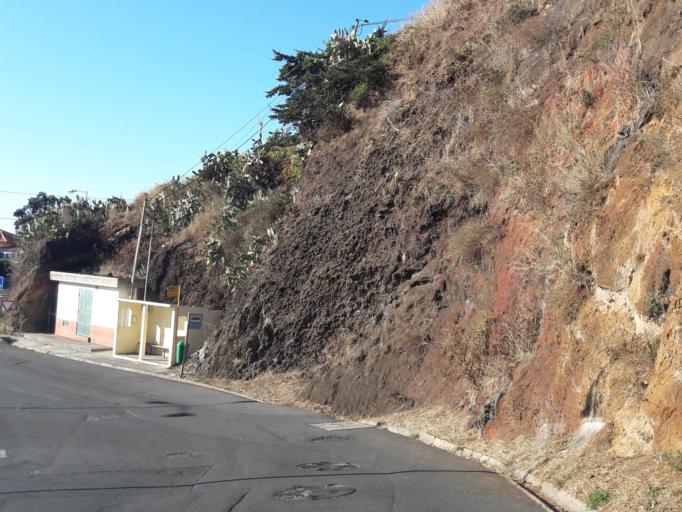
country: PT
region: Madeira
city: Canico
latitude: 32.6483
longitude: -16.8606
